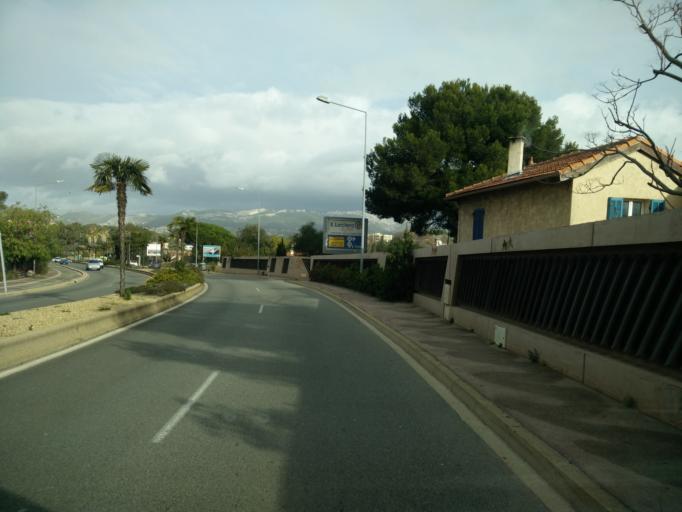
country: FR
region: Provence-Alpes-Cote d'Azur
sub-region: Departement du Var
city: Six-Fours-les-Plages
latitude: 43.1019
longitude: 5.8541
